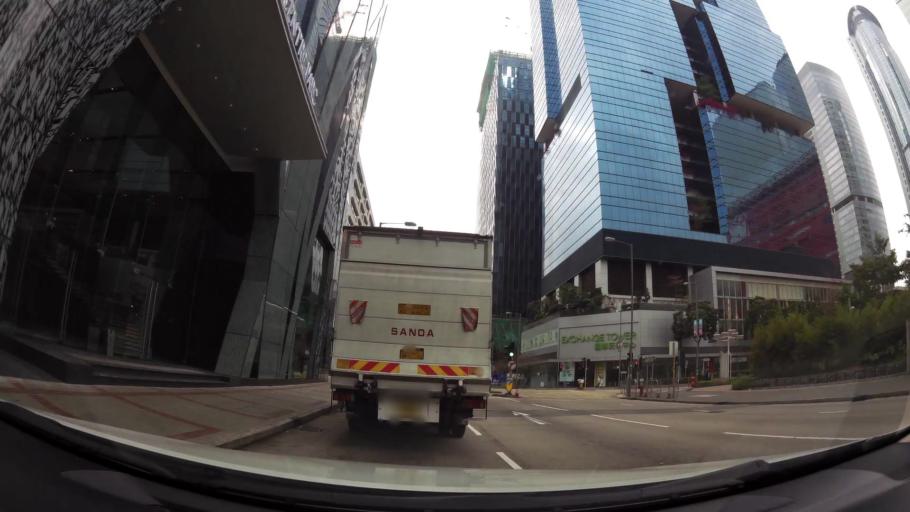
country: HK
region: Kowloon City
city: Kowloon
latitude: 22.3218
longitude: 114.2086
